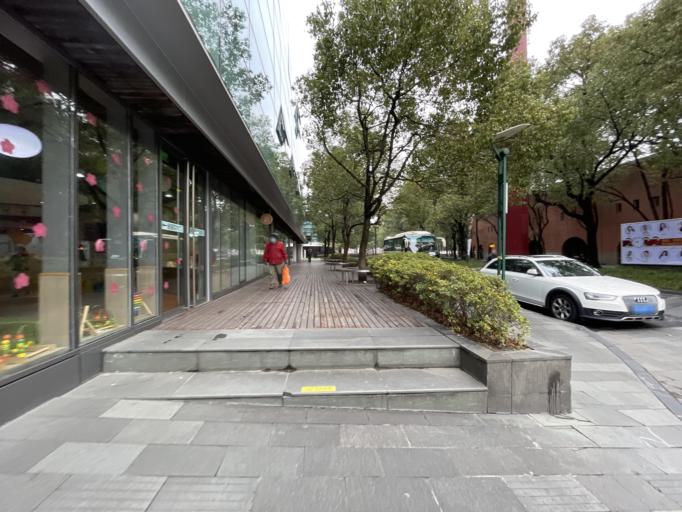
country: CN
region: Shanghai Shi
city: Yangpu
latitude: 31.3084
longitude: 121.5098
